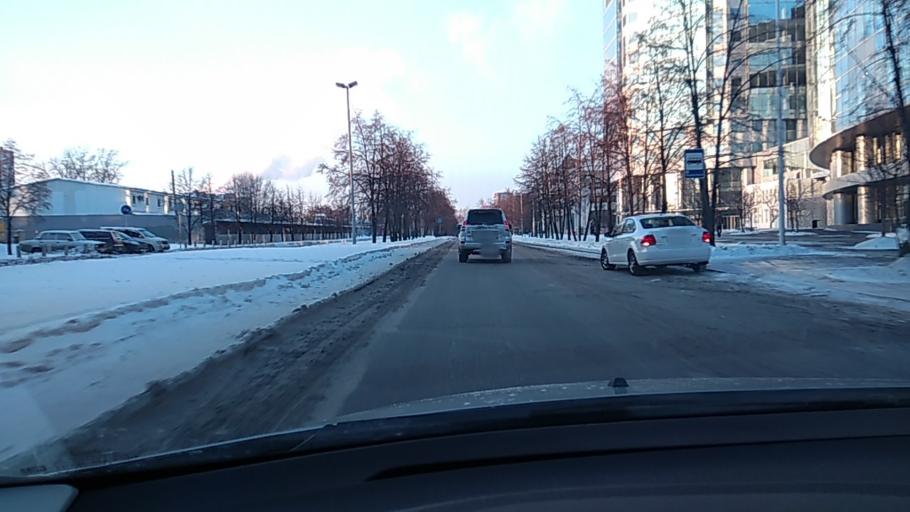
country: RU
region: Sverdlovsk
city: Yekaterinburg
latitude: 56.8440
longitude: 60.5911
